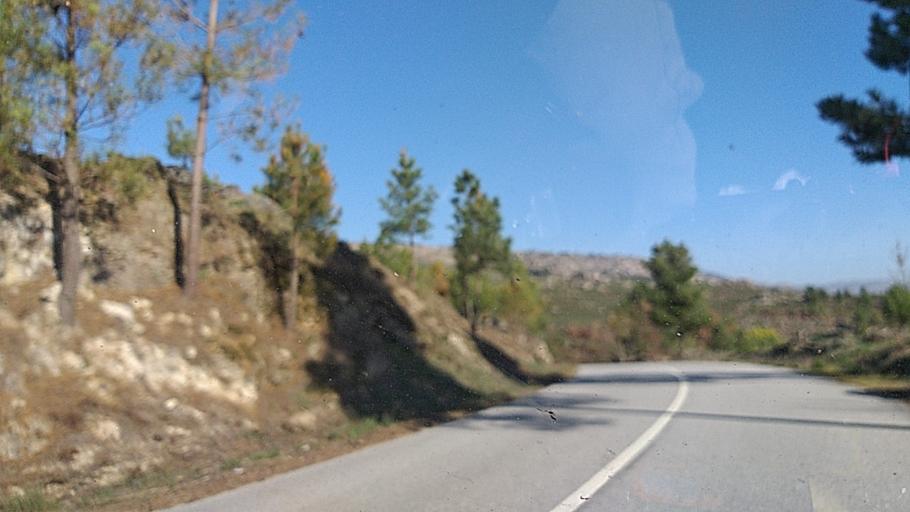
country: PT
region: Guarda
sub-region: Fornos de Algodres
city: Fornos de Algodres
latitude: 40.6447
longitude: -7.4725
